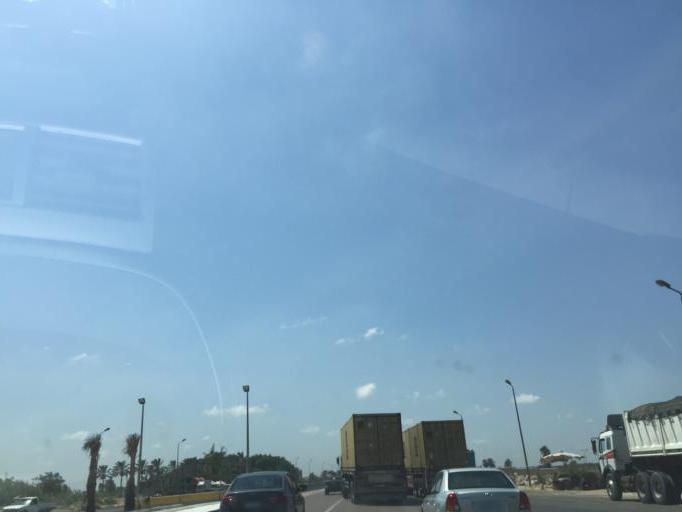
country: EG
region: Alexandria
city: Alexandria
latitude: 30.9704
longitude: 29.8265
